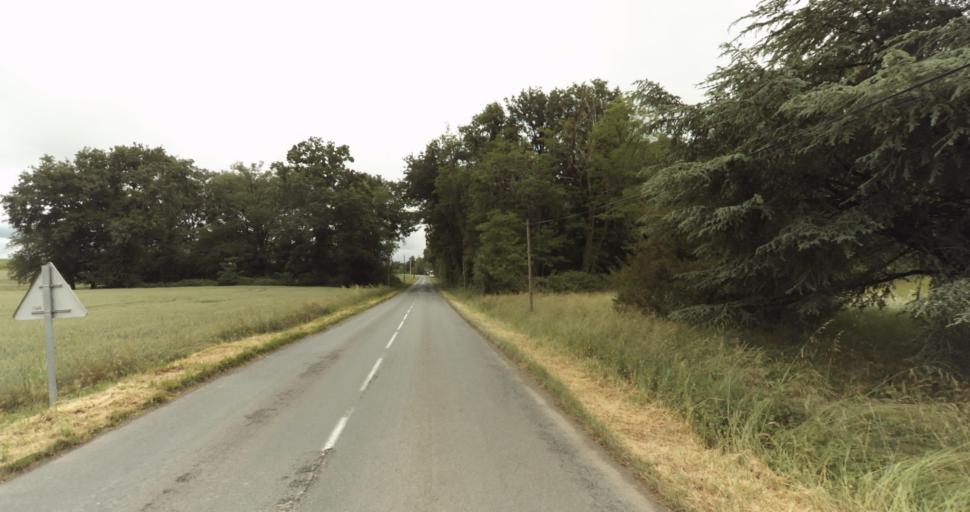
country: FR
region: Aquitaine
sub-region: Departement de la Dordogne
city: Beaumont-du-Perigord
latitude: 44.7288
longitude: 0.7902
